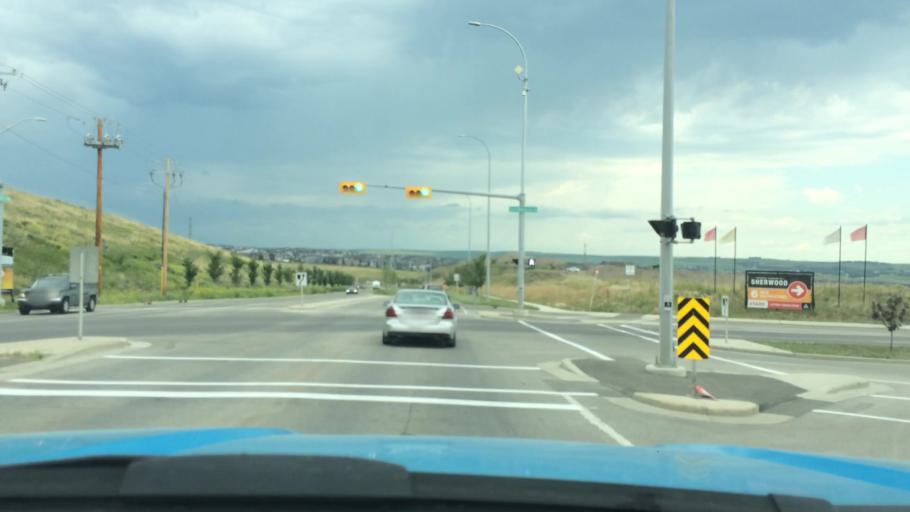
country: CA
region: Alberta
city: Calgary
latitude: 51.1624
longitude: -114.1628
